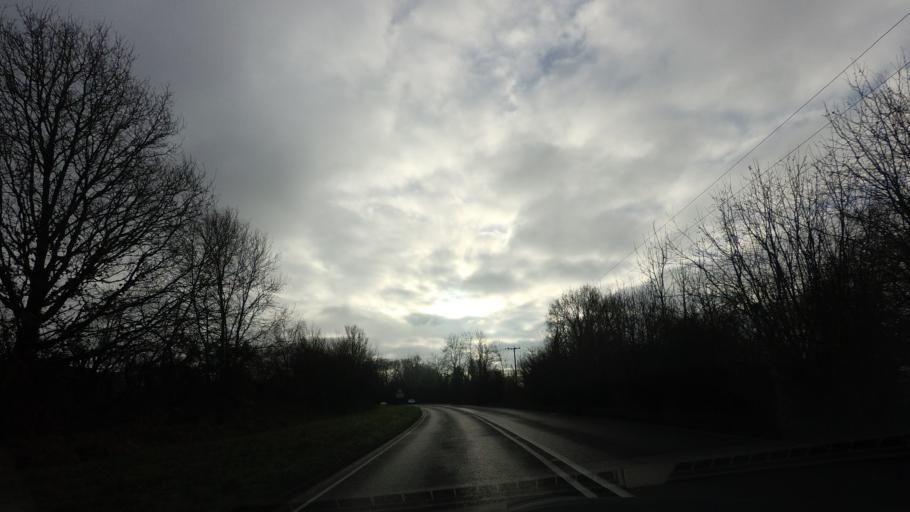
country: GB
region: England
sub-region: Kent
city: Hawkhurst
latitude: 51.0457
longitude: 0.4464
